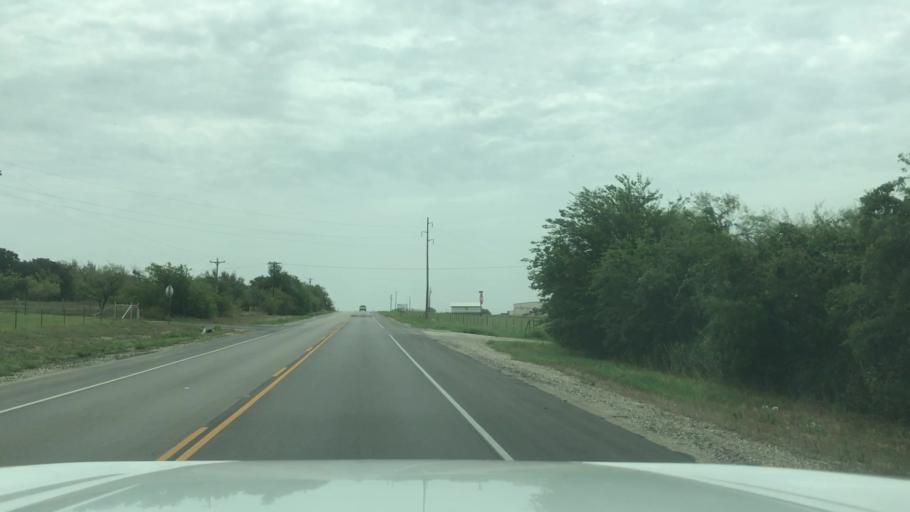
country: US
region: Texas
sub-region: Erath County
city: Dublin
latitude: 32.0880
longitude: -98.2586
